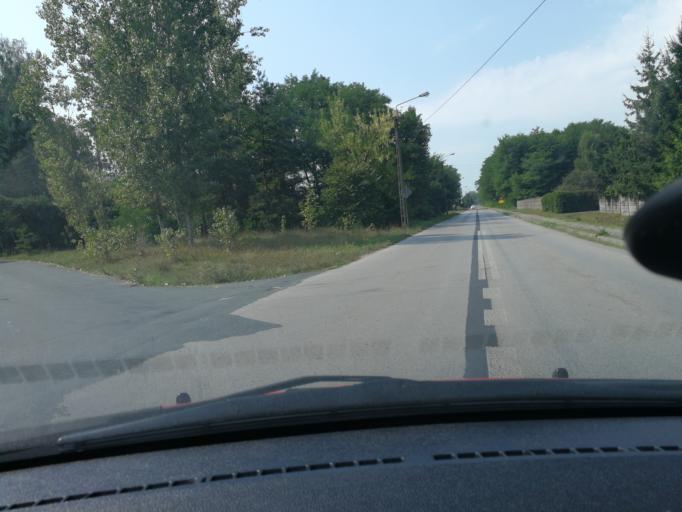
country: PL
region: Lodz Voivodeship
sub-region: powiat Lowicki
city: Bobrowniki
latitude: 52.0208
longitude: 20.0527
